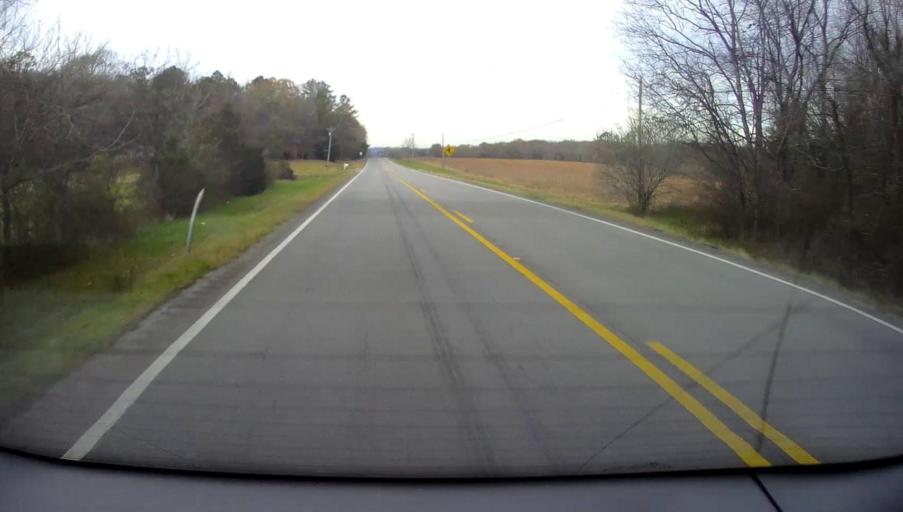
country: US
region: Alabama
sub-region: Marshall County
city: Arab
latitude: 34.3971
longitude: -86.6786
